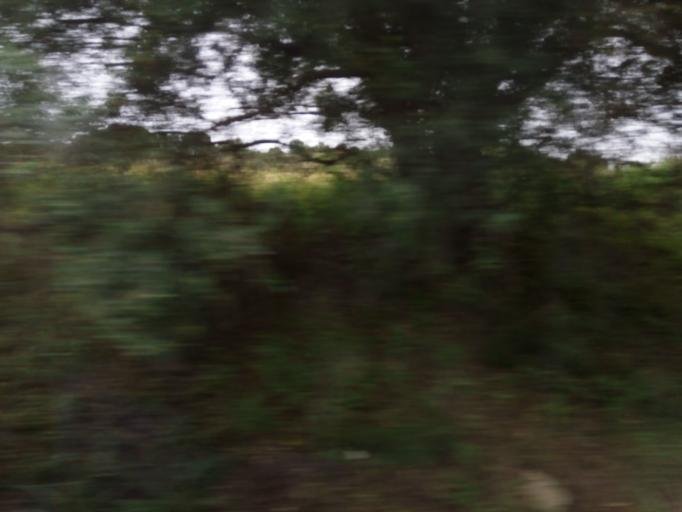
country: DZ
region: Tipaza
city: Tipasa
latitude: 36.5800
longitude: 2.5426
